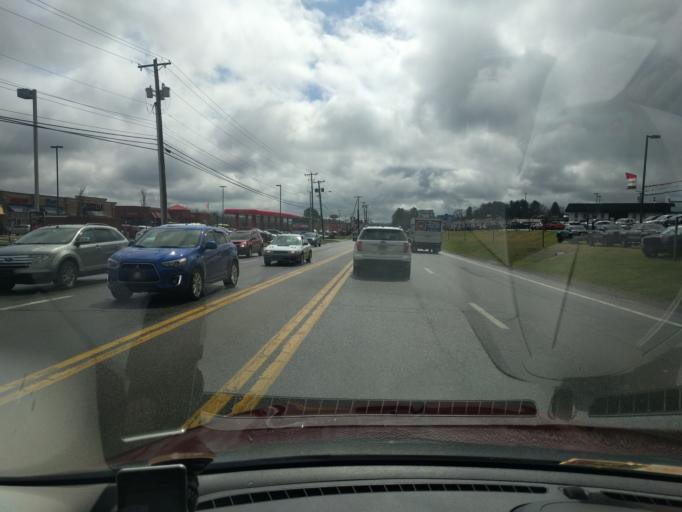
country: US
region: West Virginia
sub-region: Raleigh County
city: Beckley
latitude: 37.8053
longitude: -81.1839
